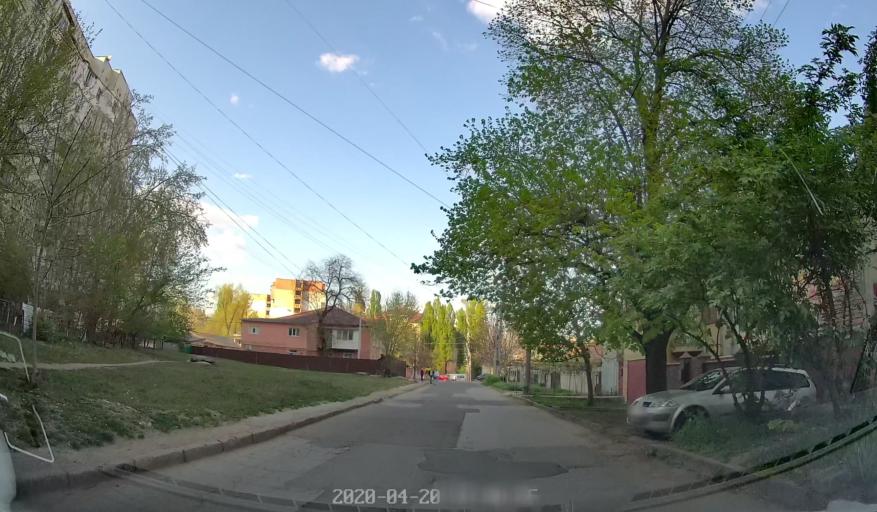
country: MD
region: Chisinau
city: Chisinau
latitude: 47.0036
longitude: 28.8620
